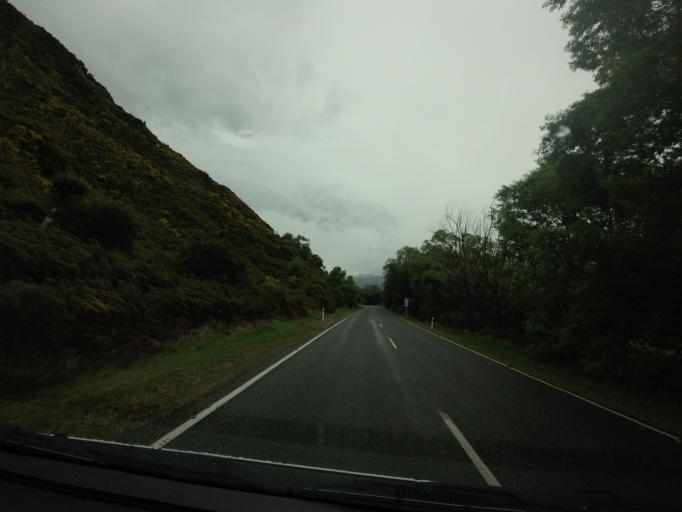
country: NZ
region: Otago
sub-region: Queenstown-Lakes District
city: Wanaka
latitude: -44.3068
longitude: 169.1971
